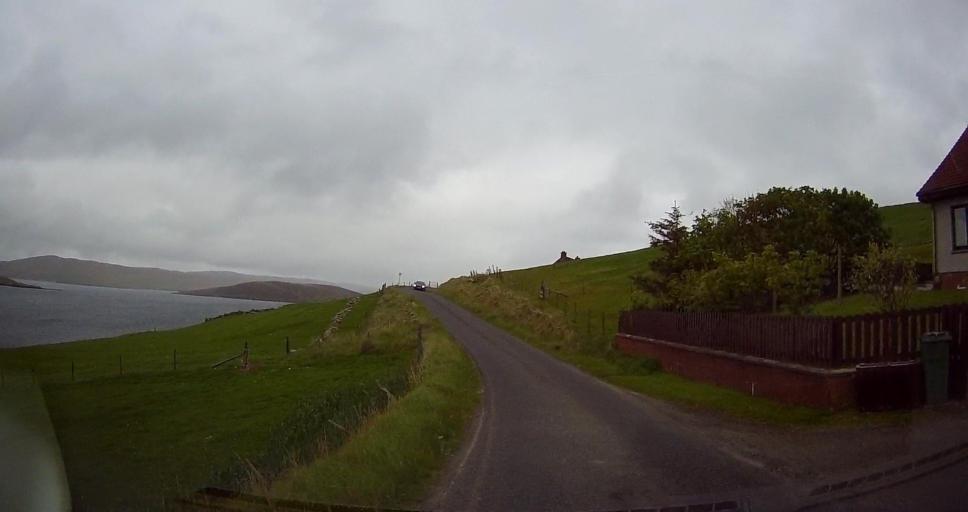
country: GB
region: Scotland
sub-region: Shetland Islands
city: Lerwick
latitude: 60.3747
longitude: -1.3829
